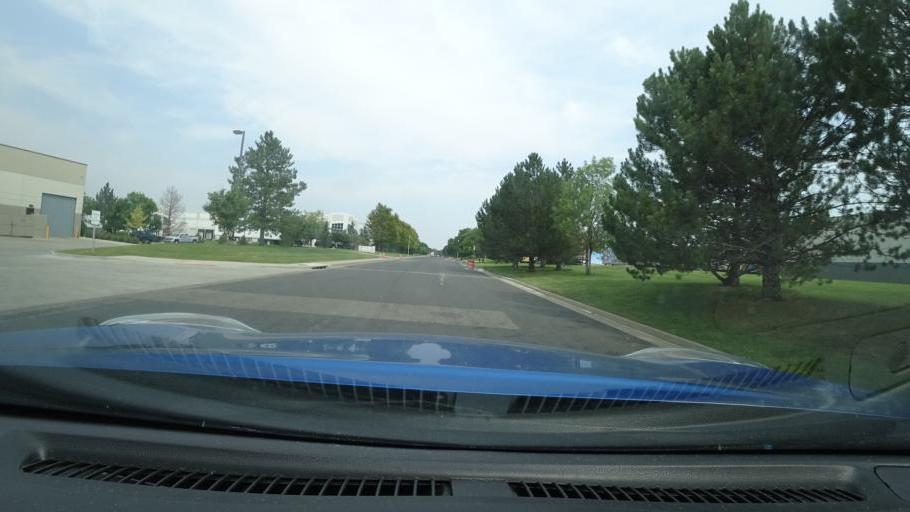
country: US
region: Colorado
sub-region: Adams County
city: Aurora
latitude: 39.7600
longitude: -104.7819
